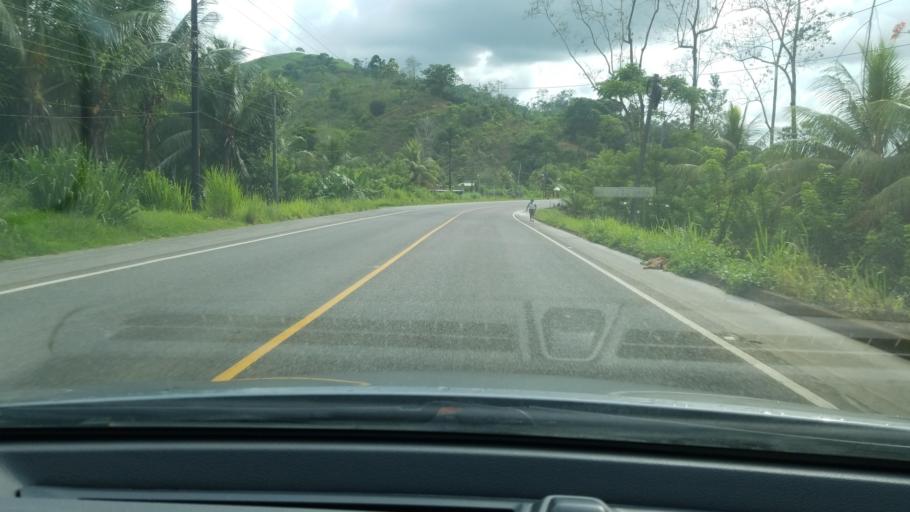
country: HN
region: Cortes
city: Potrerillos
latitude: 15.5940
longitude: -88.3082
